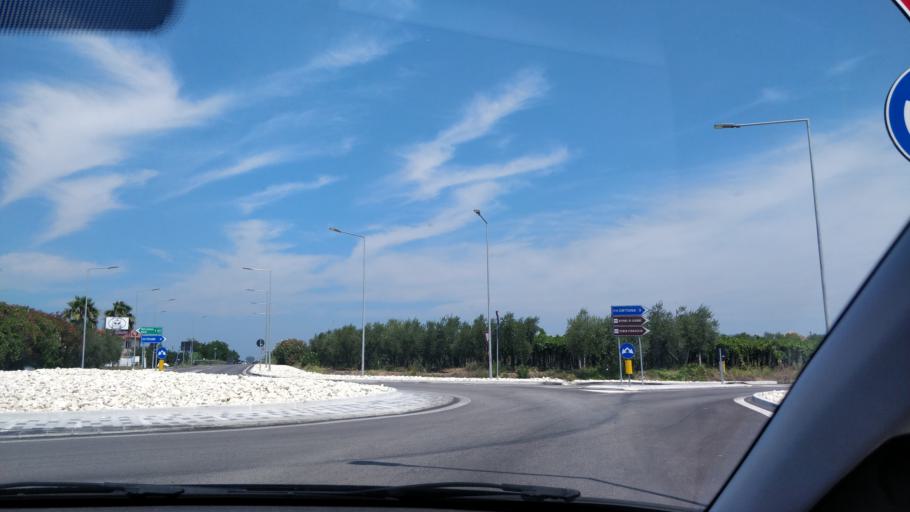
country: IT
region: Abruzzo
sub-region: Provincia di Chieti
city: Ortona
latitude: 42.3613
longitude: 14.3831
